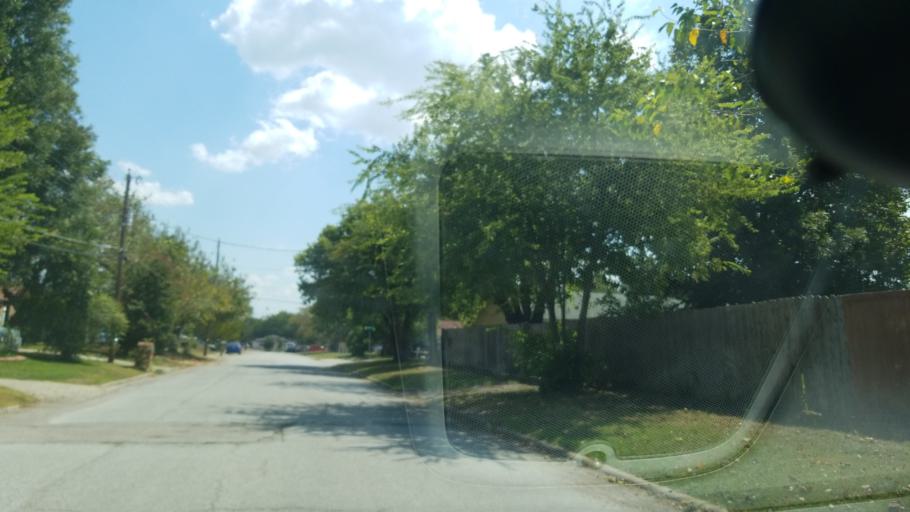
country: US
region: Texas
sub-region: Dallas County
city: Grand Prairie
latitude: 32.7153
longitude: -96.9884
